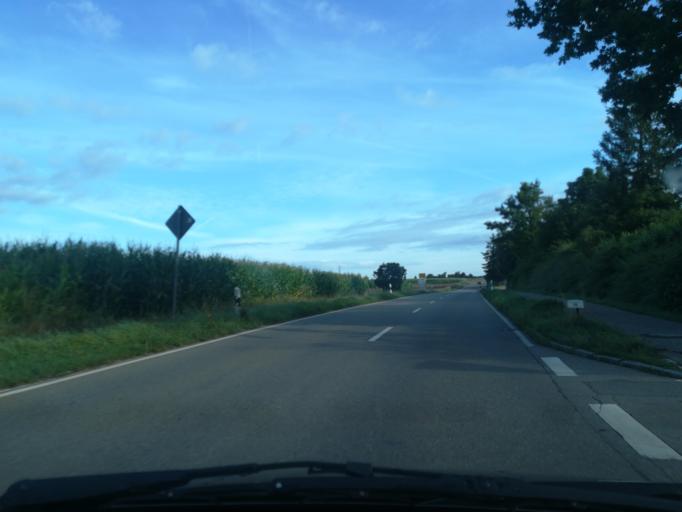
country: DE
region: Baden-Wuerttemberg
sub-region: Tuebingen Region
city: Sickenhausen
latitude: 48.5072
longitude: 9.1795
